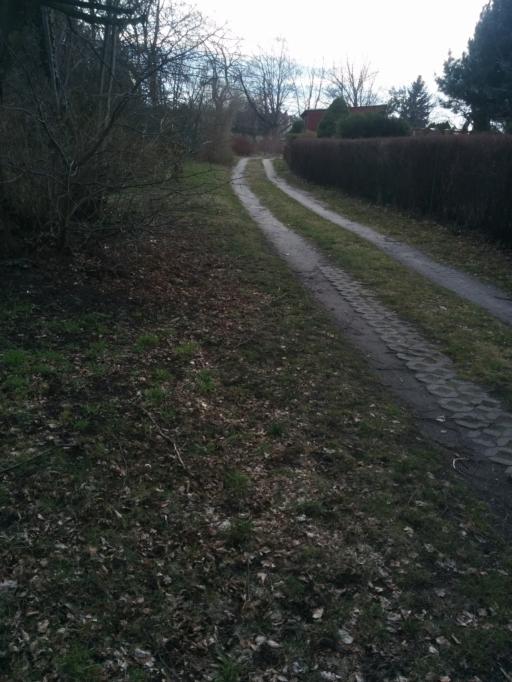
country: DE
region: Berlin
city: Adlershof
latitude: 52.4208
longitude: 13.5507
